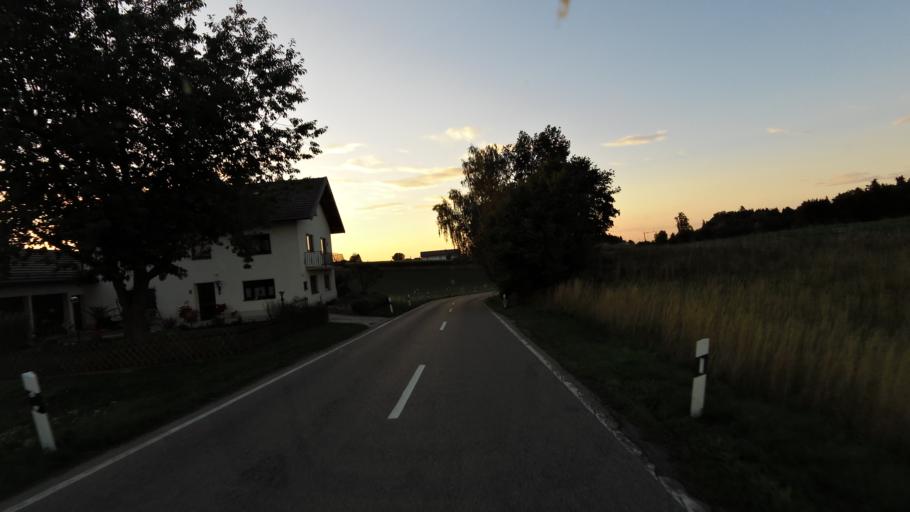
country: DE
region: Bavaria
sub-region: Upper Bavaria
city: Taufkirchen
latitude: 48.1240
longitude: 12.4638
